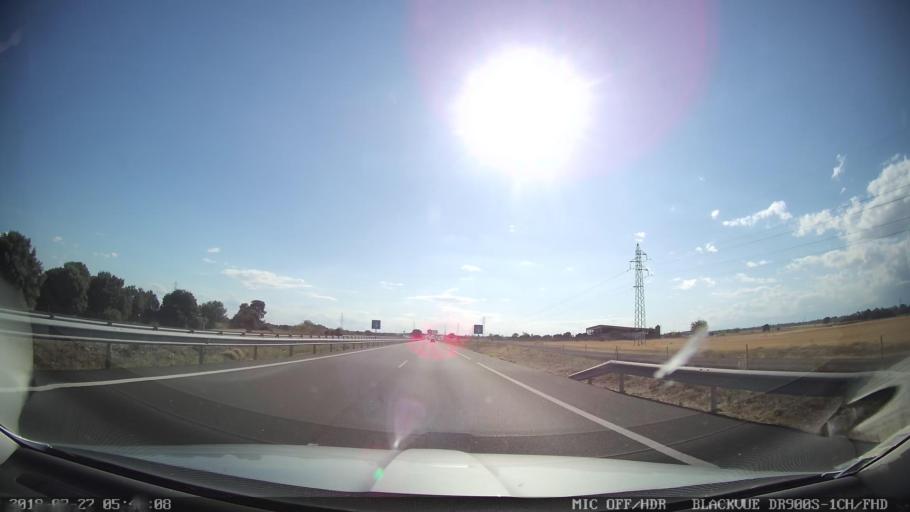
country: ES
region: Castille-La Mancha
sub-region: Province of Toledo
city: Velada
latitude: 39.9386
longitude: -4.9728
